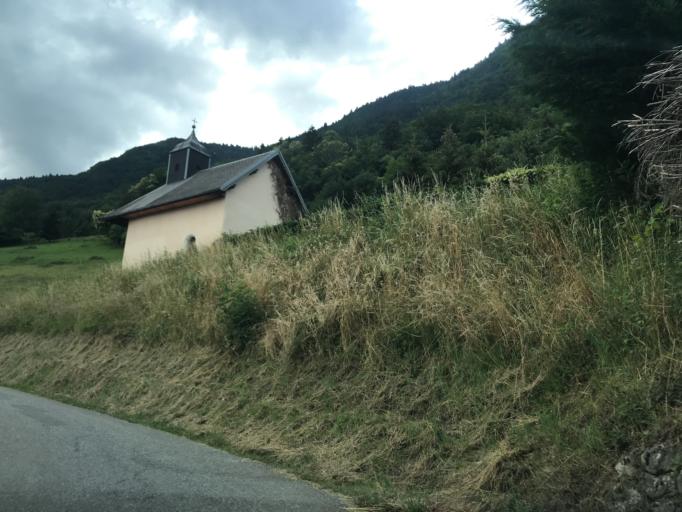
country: FR
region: Rhone-Alpes
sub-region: Departement de la Savoie
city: Mercury
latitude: 45.6809
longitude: 6.3401
